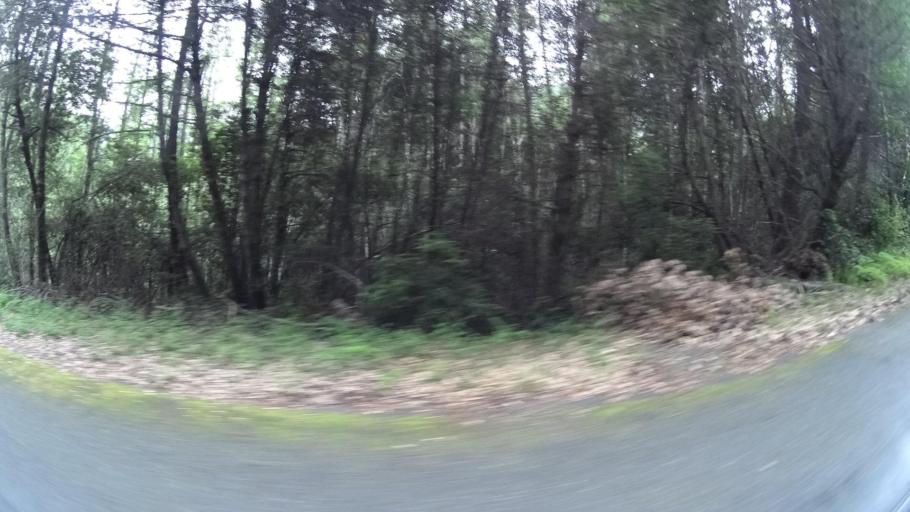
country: US
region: California
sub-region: Humboldt County
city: Willow Creek
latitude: 41.1969
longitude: -123.7578
